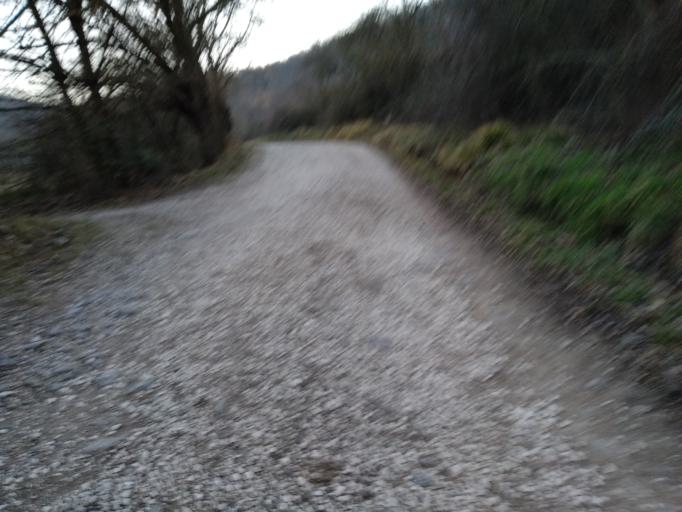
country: IT
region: Veneto
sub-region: Provincia di Padova
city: Battaglia Terme
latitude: 45.2986
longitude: 11.7733
